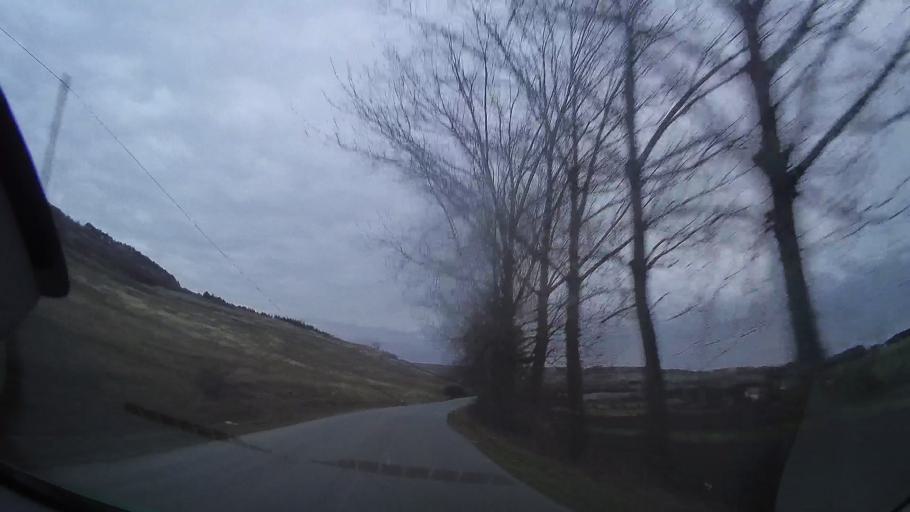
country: RO
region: Cluj
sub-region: Comuna Caianu
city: Caianu
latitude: 46.8069
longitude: 23.9296
